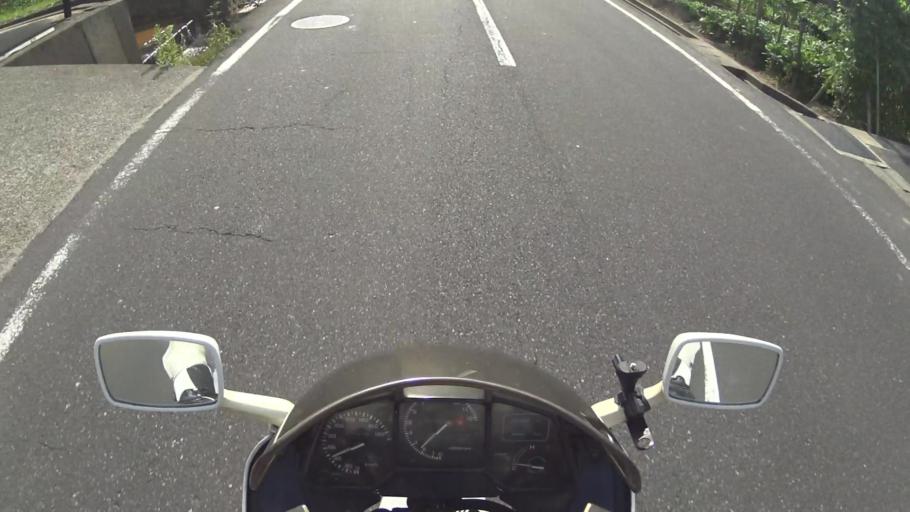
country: JP
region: Kyoto
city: Miyazu
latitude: 35.5852
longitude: 135.1002
